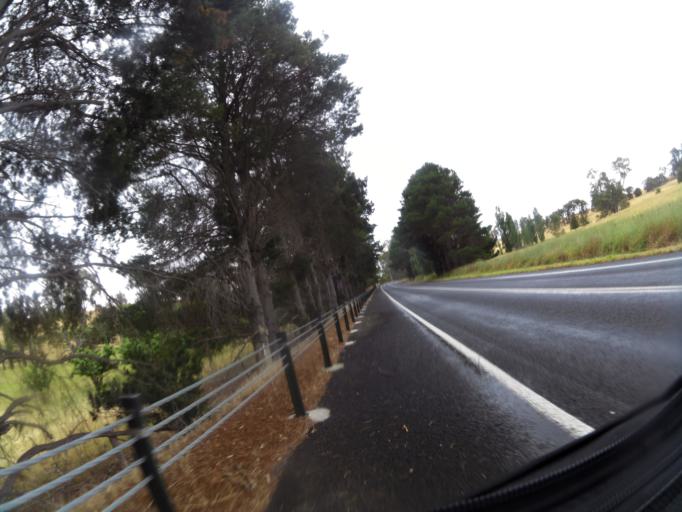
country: AU
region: Victoria
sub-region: Mount Alexander
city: Castlemaine
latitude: -37.1808
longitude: 144.0276
